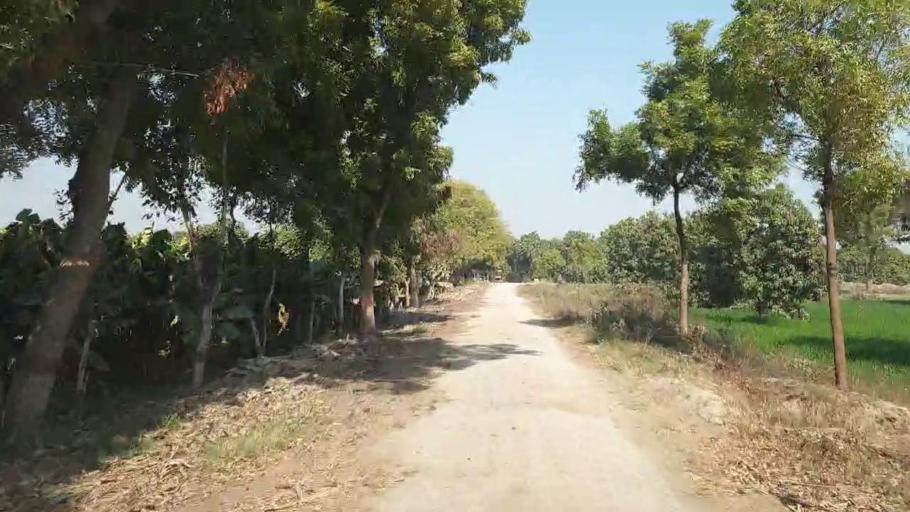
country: PK
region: Sindh
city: Tando Jam
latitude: 25.3430
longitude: 68.6139
